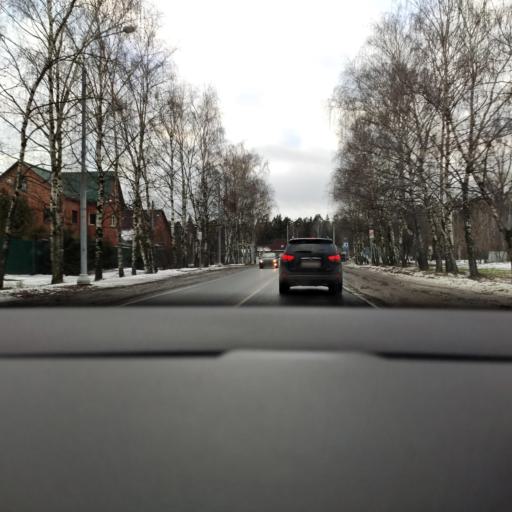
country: RU
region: Moskovskaya
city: Lesnyye Polyany
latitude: 55.9584
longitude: 37.8561
